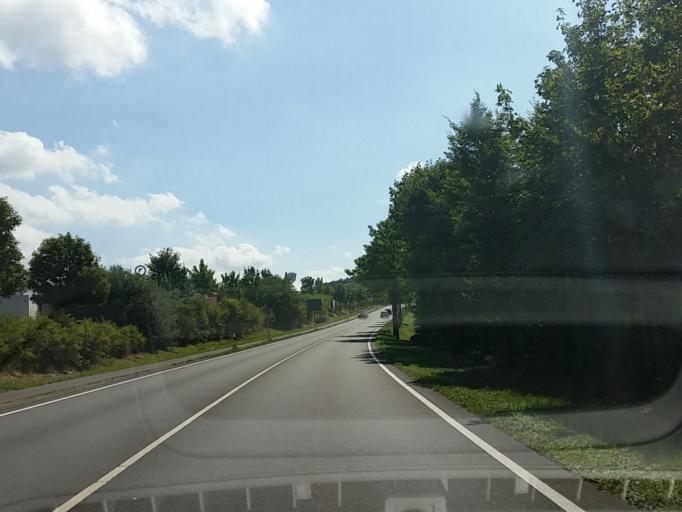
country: DE
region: Saarland
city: Schmelz
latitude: 49.4393
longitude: 6.8737
